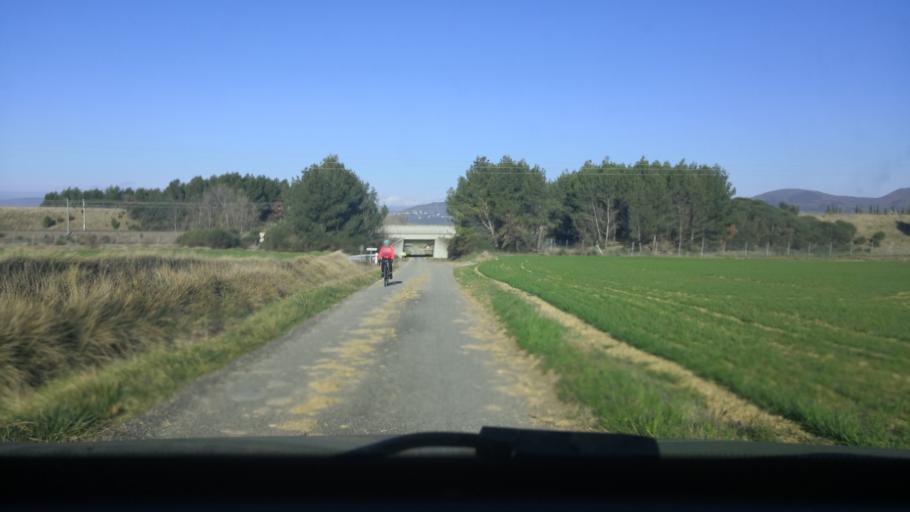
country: FR
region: Rhone-Alpes
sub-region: Departement de la Drome
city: Sauzet
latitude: 44.5688
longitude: 4.8464
